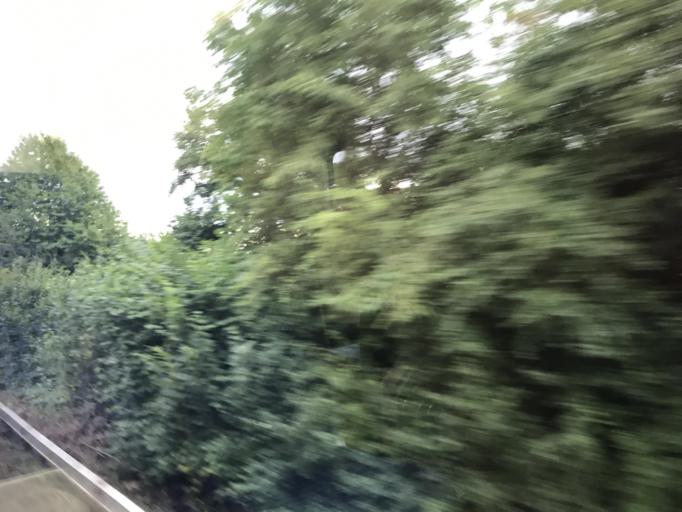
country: DE
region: Rheinland-Pfalz
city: Niederirsen
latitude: 50.8106
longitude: 7.5638
